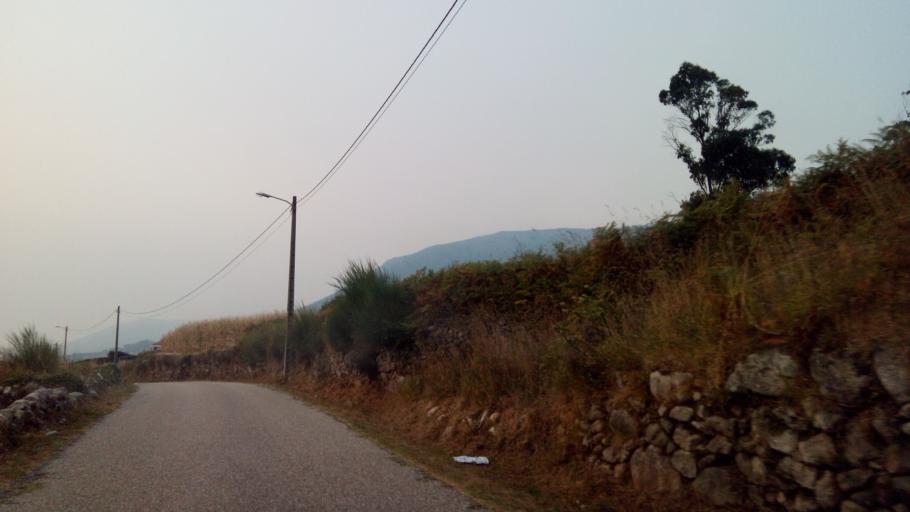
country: ES
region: Galicia
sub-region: Provincia de Pontevedra
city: Oia
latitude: 41.9937
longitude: -8.8801
